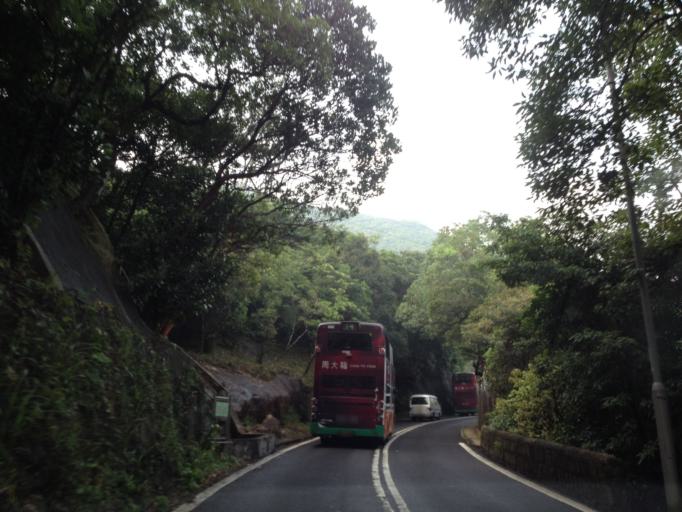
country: HK
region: Wanchai
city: Wan Chai
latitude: 22.2613
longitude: 114.2255
